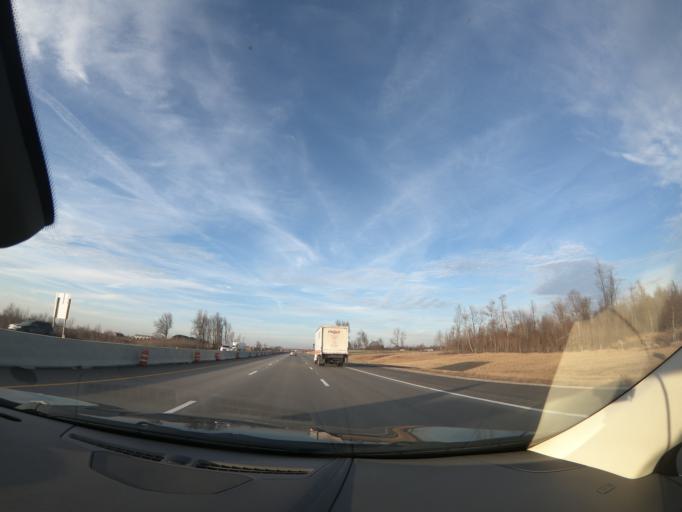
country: US
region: Kentucky
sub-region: Larue County
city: Hodgenville
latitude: 37.5335
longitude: -85.8821
